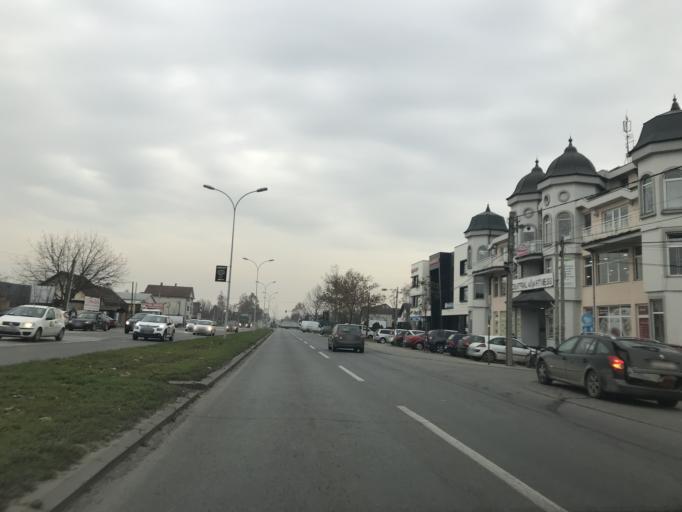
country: RS
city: Veternik
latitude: 45.2474
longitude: 19.7650
